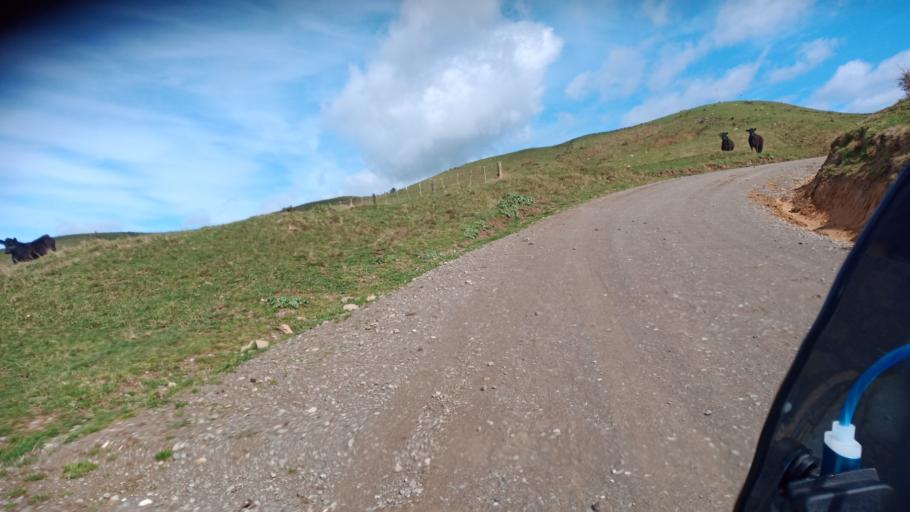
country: NZ
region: Hawke's Bay
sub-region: Wairoa District
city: Wairoa
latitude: -38.7370
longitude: 177.3061
